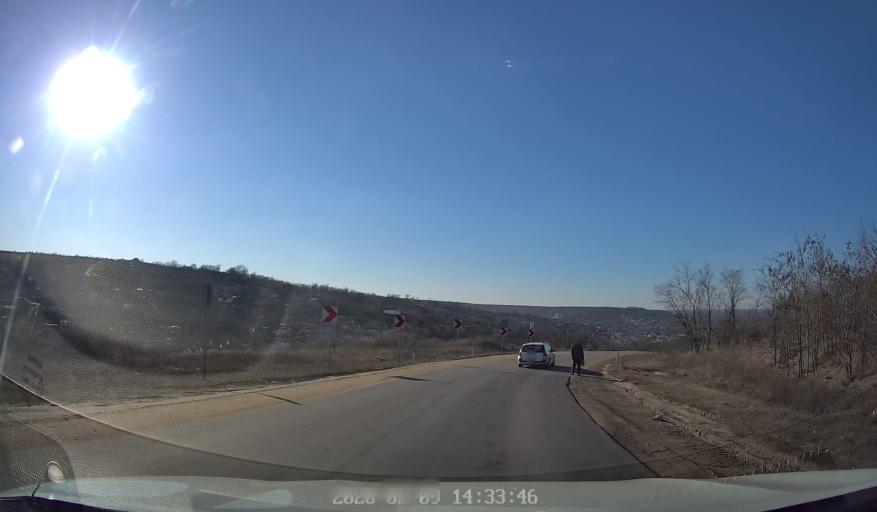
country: MD
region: Causeni
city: Causeni
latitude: 46.6345
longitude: 29.4257
